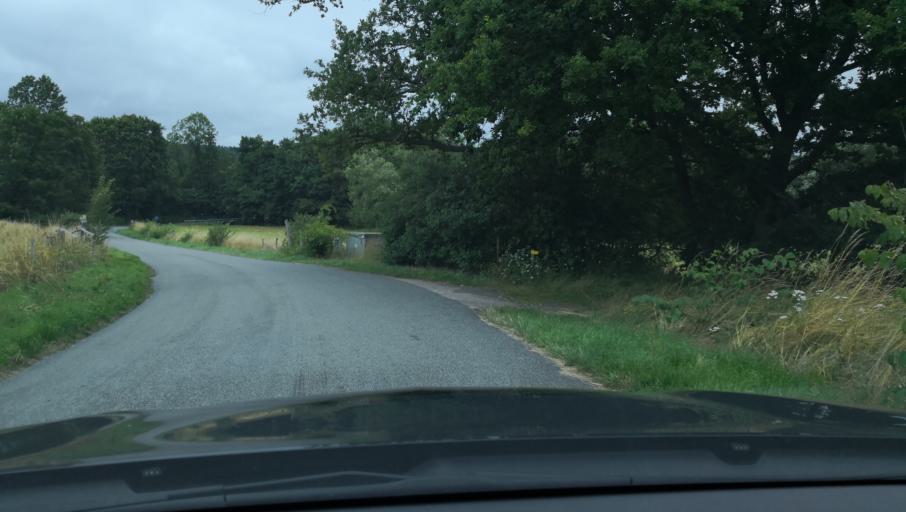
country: SE
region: Skane
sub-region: Simrishamns Kommun
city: Kivik
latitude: 55.7193
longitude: 14.1570
